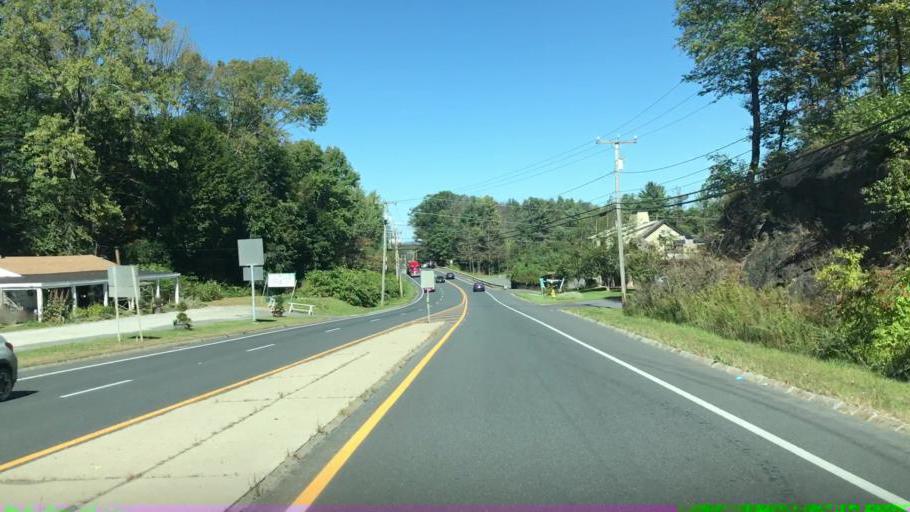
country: US
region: Massachusetts
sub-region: Berkshire County
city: Pittsfield
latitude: 42.4116
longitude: -73.2621
